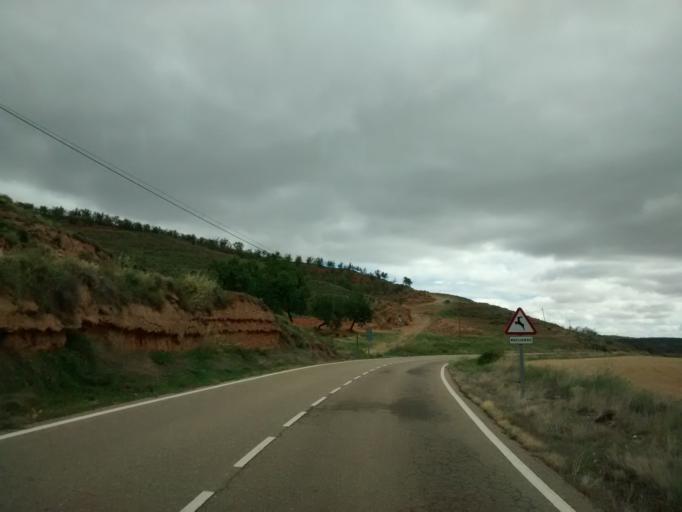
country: ES
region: Aragon
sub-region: Provincia de Zaragoza
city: Trasmoz
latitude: 41.8309
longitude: -1.7232
